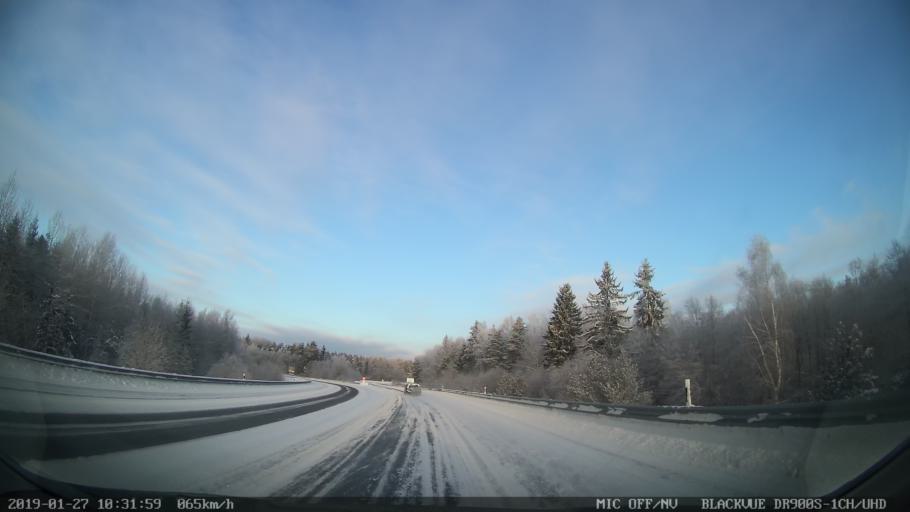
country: EE
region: Harju
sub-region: Raasiku vald
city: Raasiku
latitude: 59.4368
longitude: 25.1896
